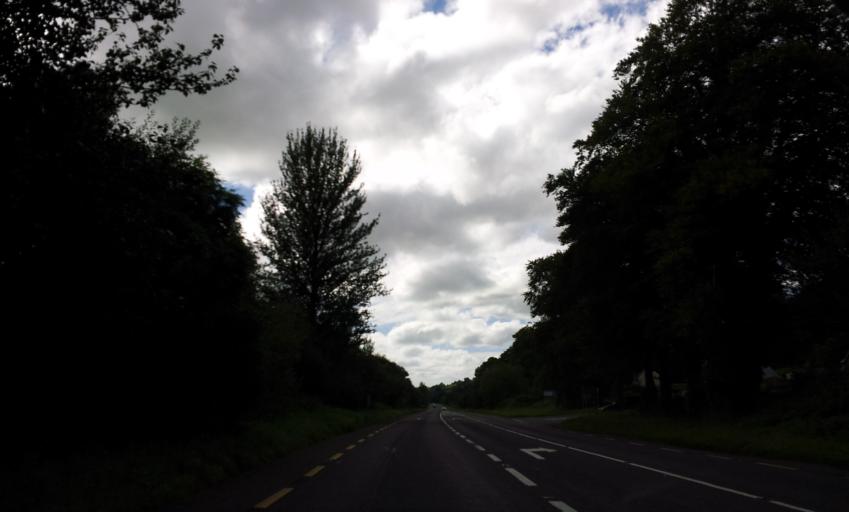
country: IE
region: Munster
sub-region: County Cork
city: Bandon
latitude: 51.8609
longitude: -8.7861
